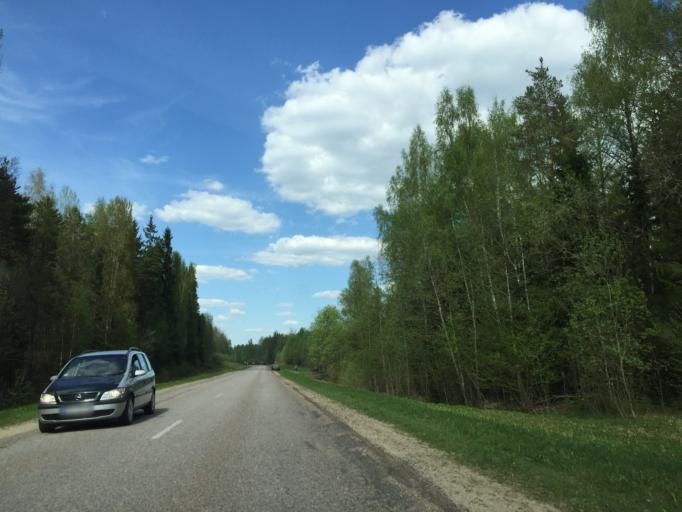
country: LV
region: Limbazu Rajons
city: Limbazi
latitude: 57.4187
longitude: 24.7018
